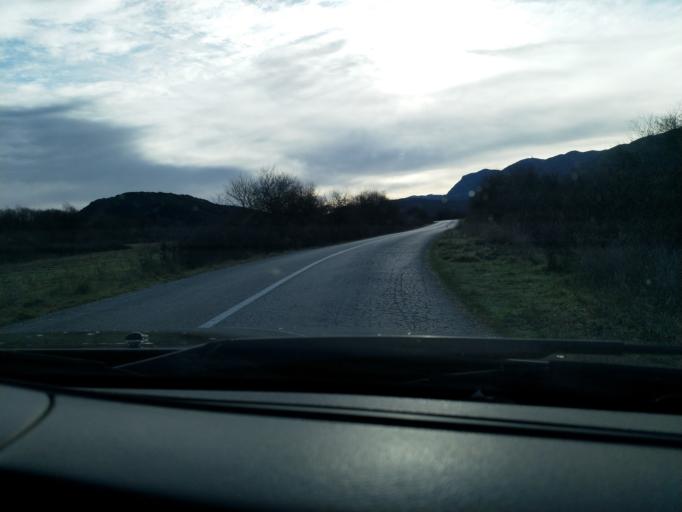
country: GR
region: Epirus
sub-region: Nomos Ioanninon
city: Asprangeloi
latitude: 39.8690
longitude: 20.7117
